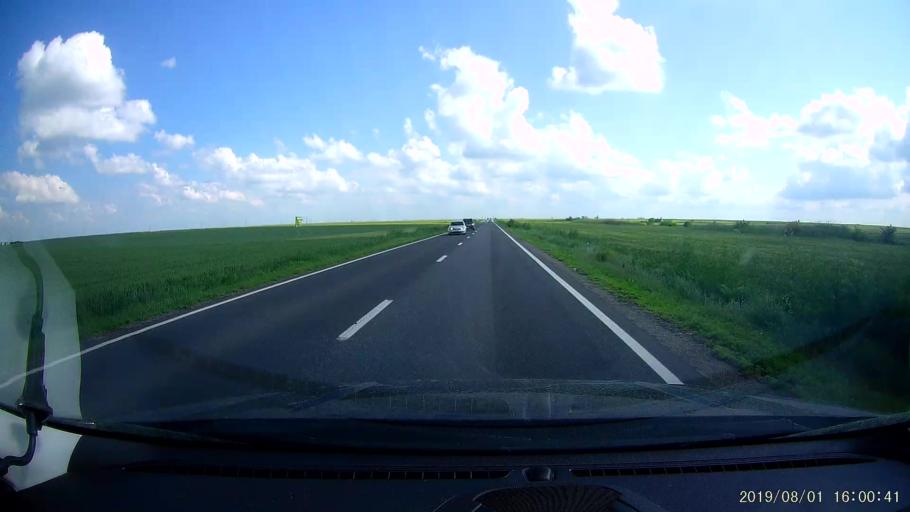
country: RO
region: Ialomita
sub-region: Comuna Ciulnita
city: Ciulnita
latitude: 44.5232
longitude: 27.3892
